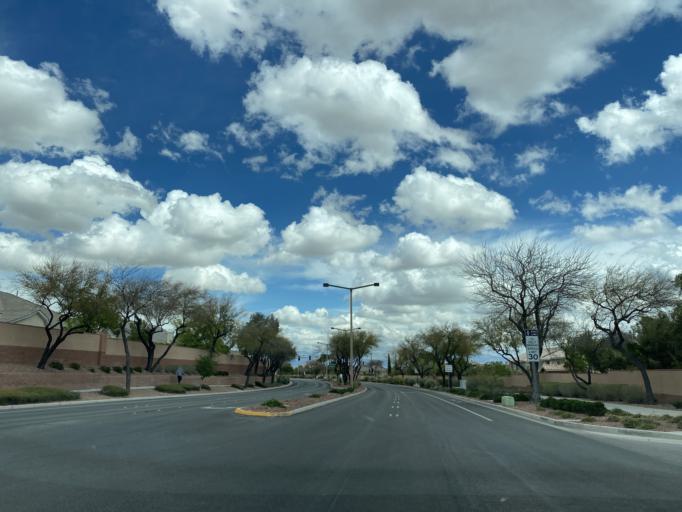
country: US
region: Nevada
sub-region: Clark County
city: Summerlin South
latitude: 36.1837
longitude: -115.3297
